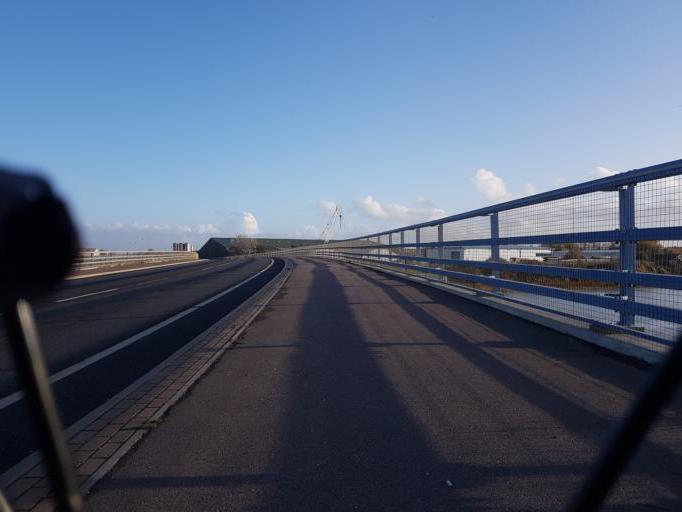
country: GB
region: England
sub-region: Kent
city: Sittingbourne
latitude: 51.3537
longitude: 0.7553
